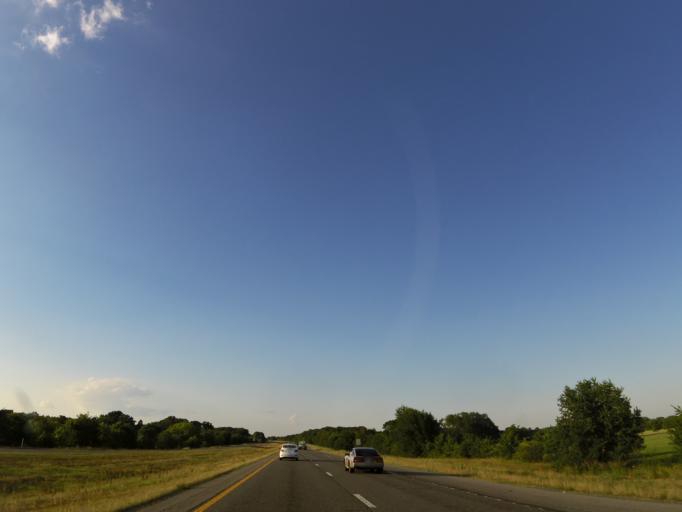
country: US
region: Tennessee
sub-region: Rutherford County
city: Murfreesboro
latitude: 35.9138
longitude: -86.4406
